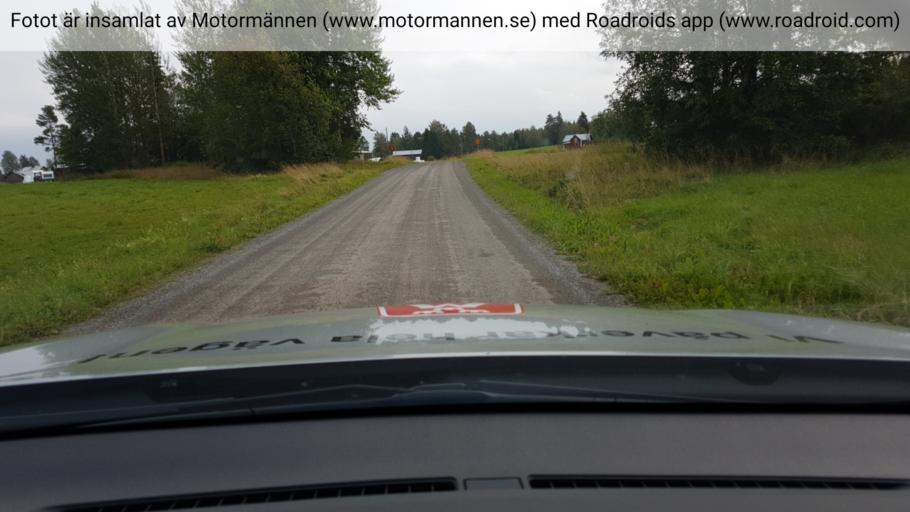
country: SE
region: Jaemtland
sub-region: Stroemsunds Kommun
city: Stroemsund
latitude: 63.7297
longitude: 15.4766
